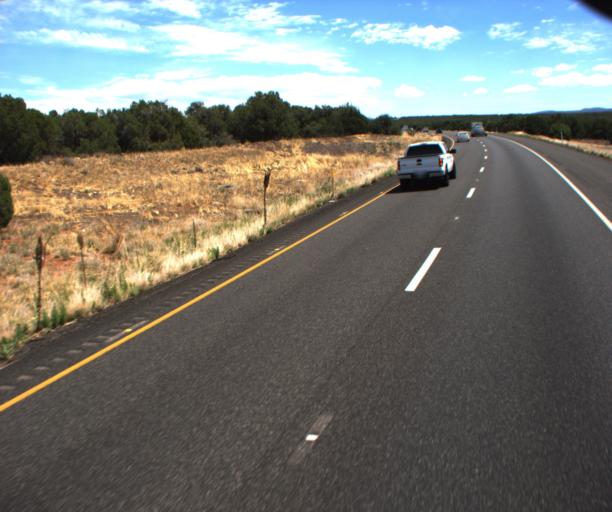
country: US
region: Arizona
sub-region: Yavapai County
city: Big Park
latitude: 34.7316
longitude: -111.7017
